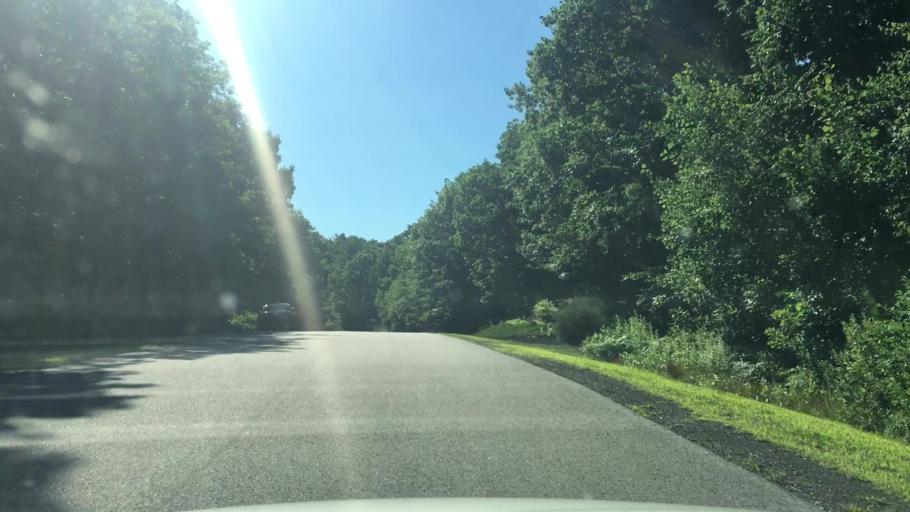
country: US
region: New Hampshire
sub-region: Rockingham County
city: Newmarket
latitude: 43.0362
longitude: -70.9604
